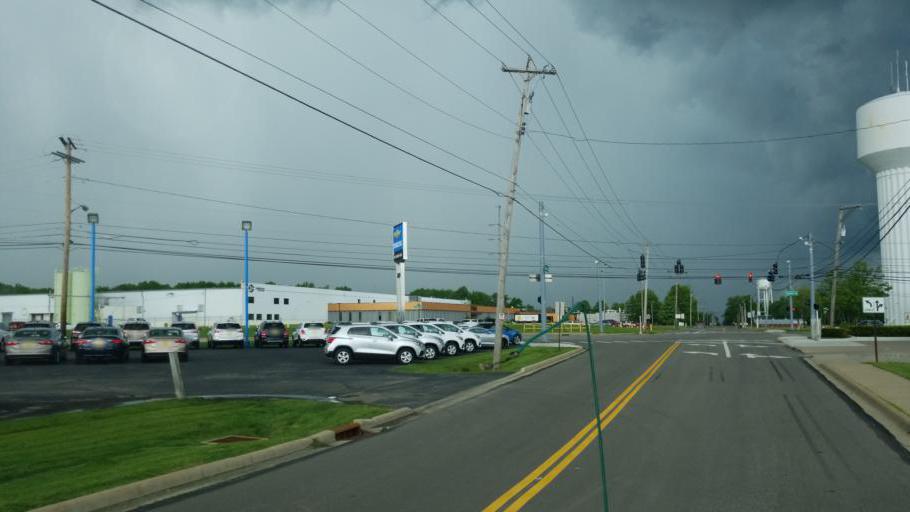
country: US
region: Ohio
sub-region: Ashland County
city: Ashland
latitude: 40.8463
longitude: -82.3491
